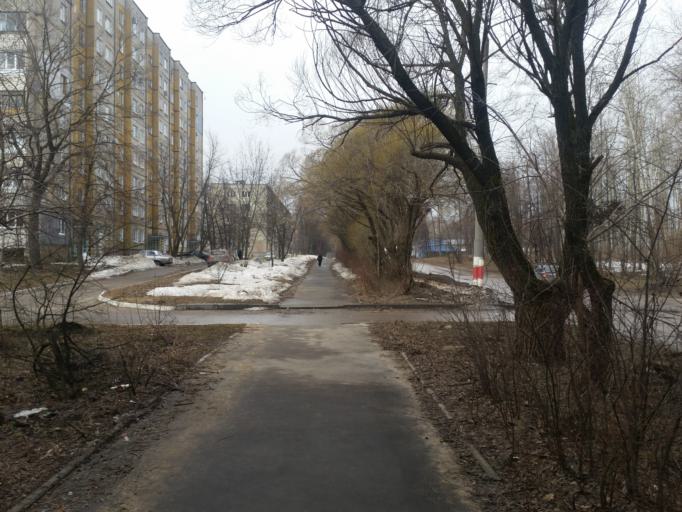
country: RU
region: Ulyanovsk
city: Dimitrovgrad
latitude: 54.2380
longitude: 49.5514
